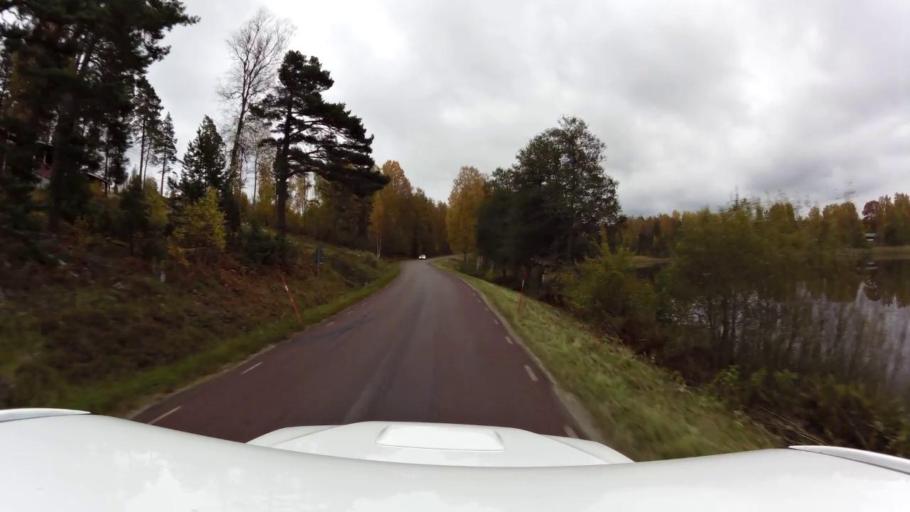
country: SE
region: OEstergoetland
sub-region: Linkopings Kommun
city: Ljungsbro
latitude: 58.5711
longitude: 15.5131
